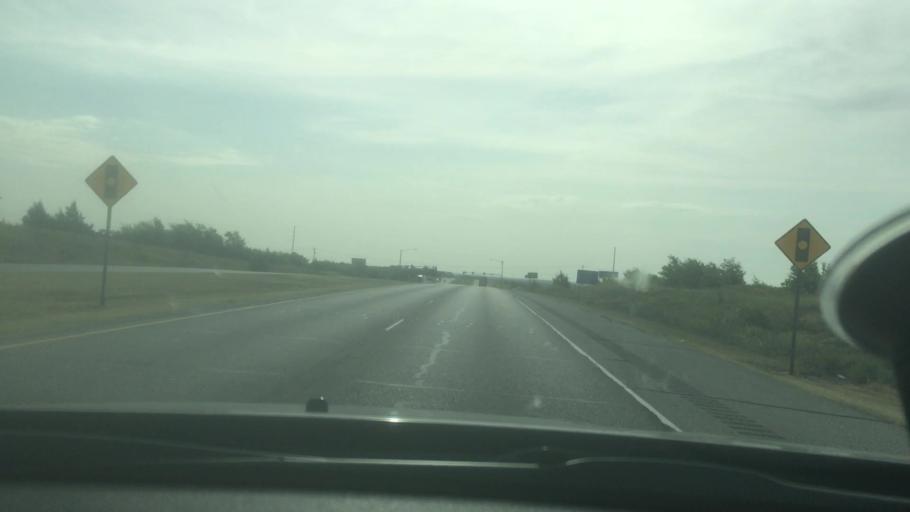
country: US
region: Oklahoma
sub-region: Carter County
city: Ardmore
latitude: 34.1392
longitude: -97.1468
